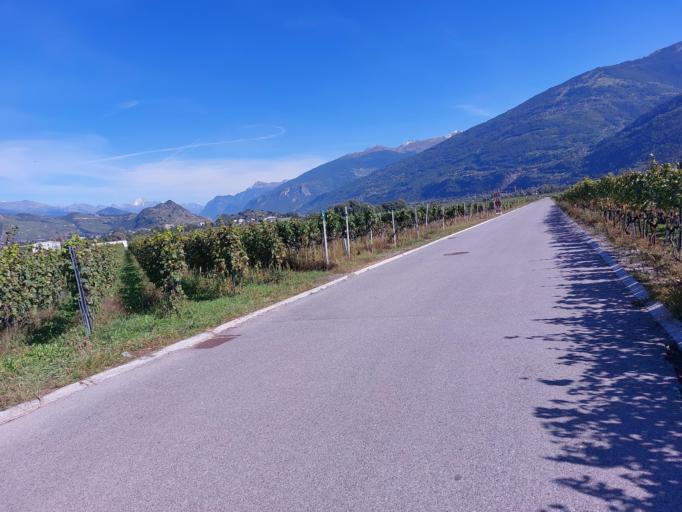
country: CH
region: Valais
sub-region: Conthey District
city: Ardon
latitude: 46.2134
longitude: 7.2713
